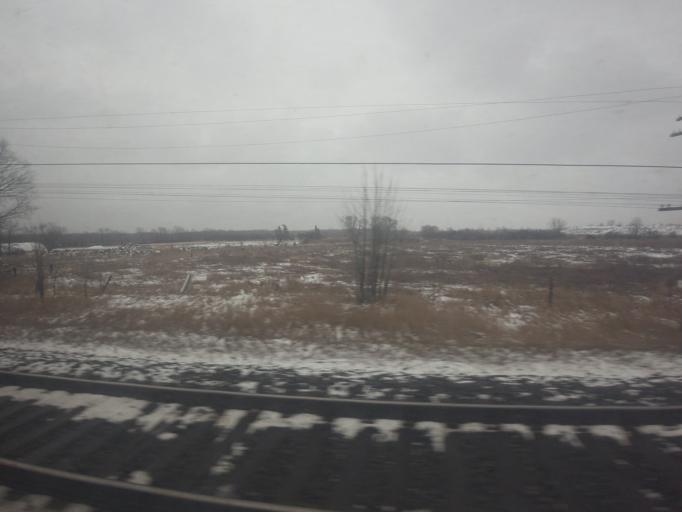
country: CA
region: Ontario
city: Quinte West
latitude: 44.1376
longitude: -77.5338
